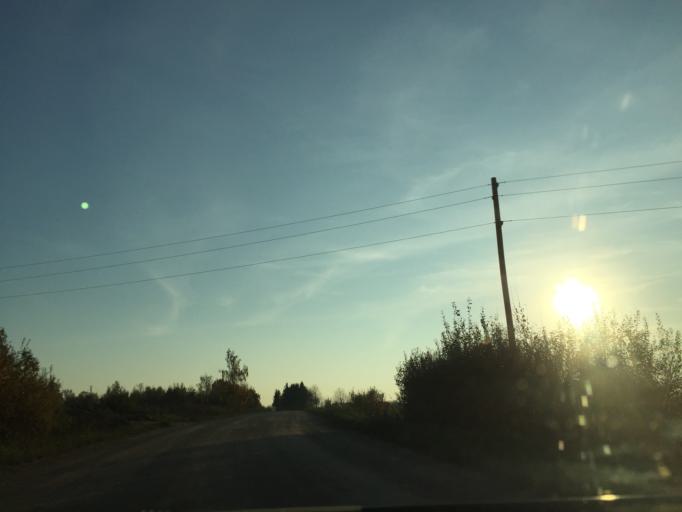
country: LV
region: Vainode
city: Vainode
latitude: 56.5520
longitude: 21.8427
